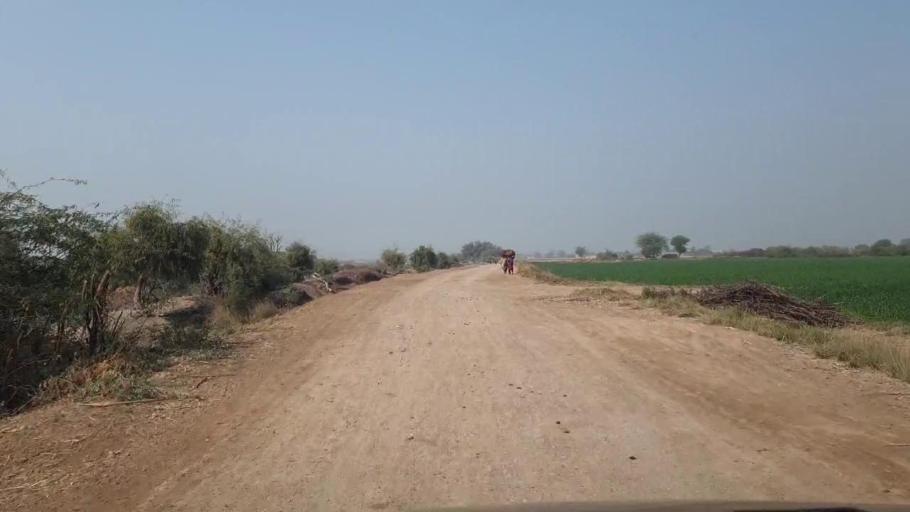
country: PK
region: Sindh
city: Hala
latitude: 25.9784
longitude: 68.4274
